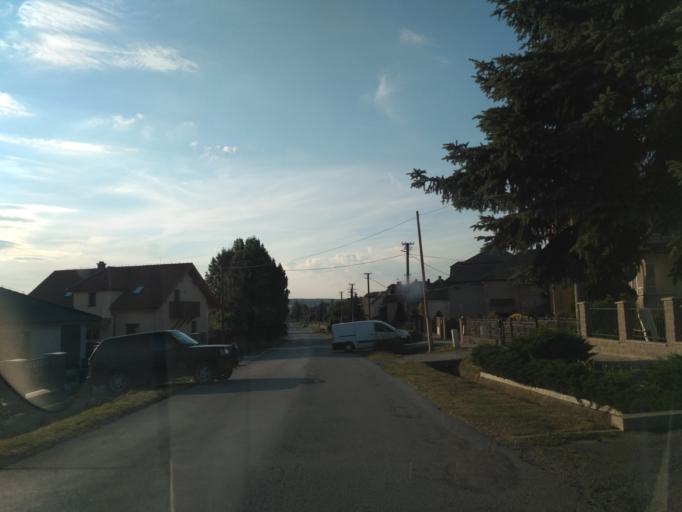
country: SK
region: Kosicky
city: Kosice
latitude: 48.7330
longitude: 21.4416
